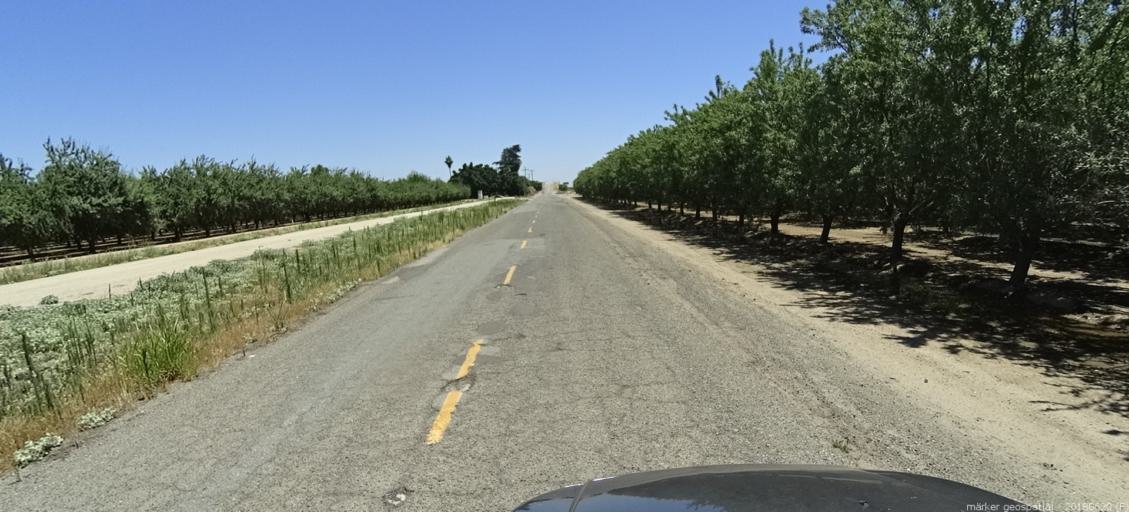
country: US
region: California
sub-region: Fresno County
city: Biola
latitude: 36.8658
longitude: -119.9674
